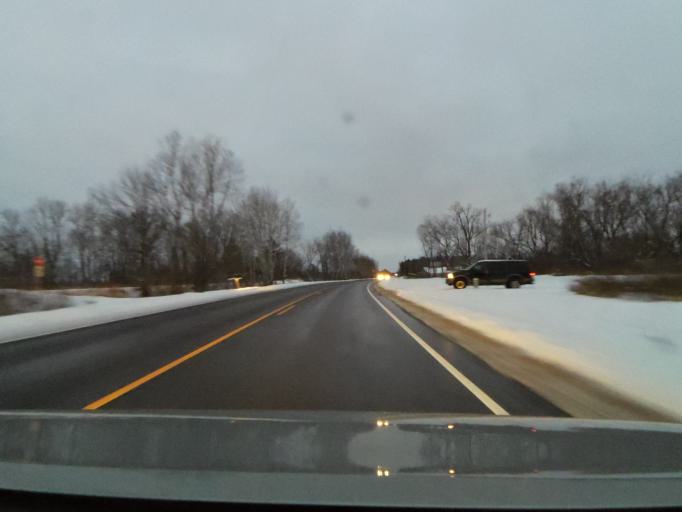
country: US
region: Wisconsin
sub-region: Dunn County
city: Menomonie
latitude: 44.9275
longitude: -91.9842
